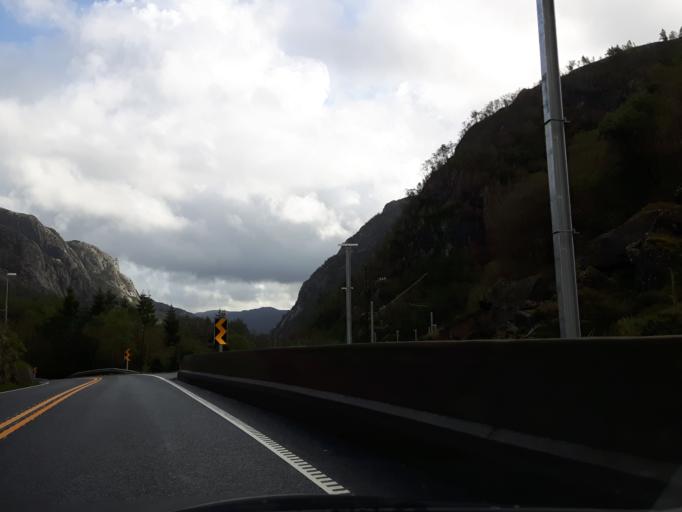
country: NO
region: Rogaland
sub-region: Lund
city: Moi
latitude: 58.4701
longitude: 6.3962
